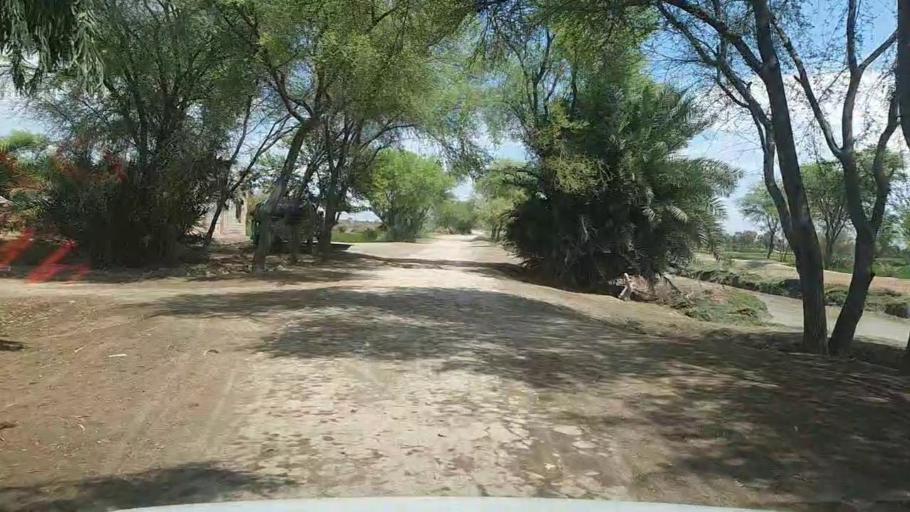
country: PK
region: Sindh
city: Kandhkot
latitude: 28.3405
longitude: 69.2438
